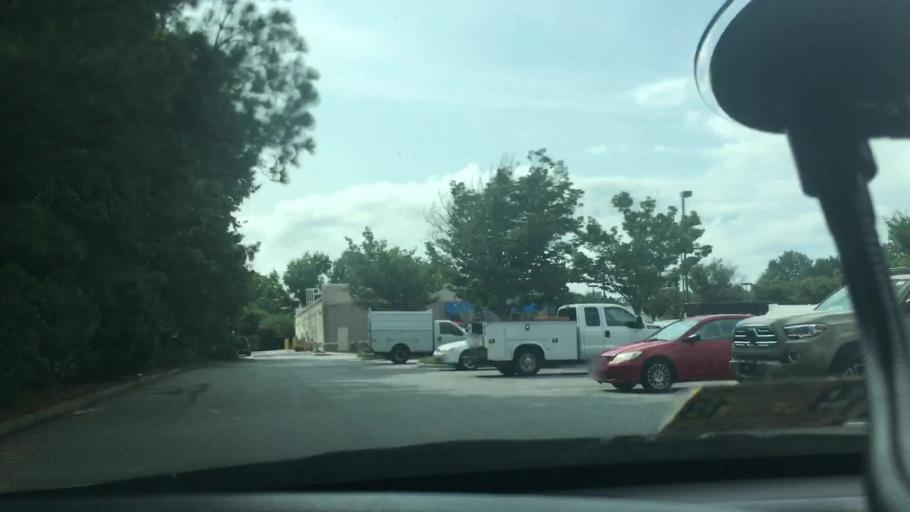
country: US
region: Virginia
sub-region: City of Virginia Beach
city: Virginia Beach
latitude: 36.9028
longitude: -76.1314
